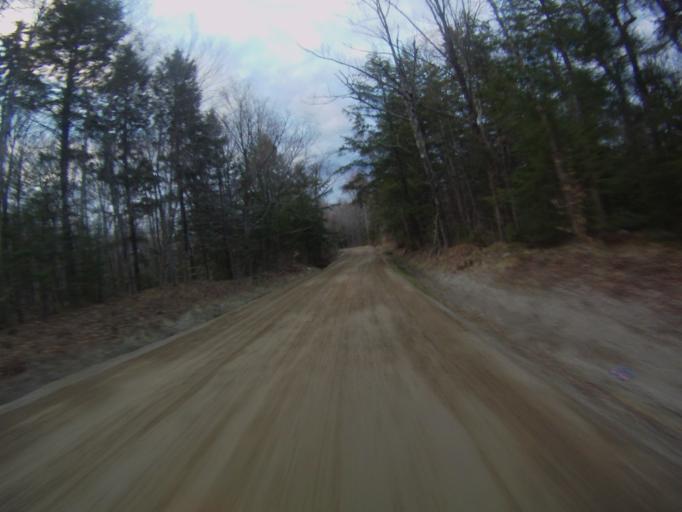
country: US
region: Vermont
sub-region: Rutland County
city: Brandon
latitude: 43.9352
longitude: -73.0208
